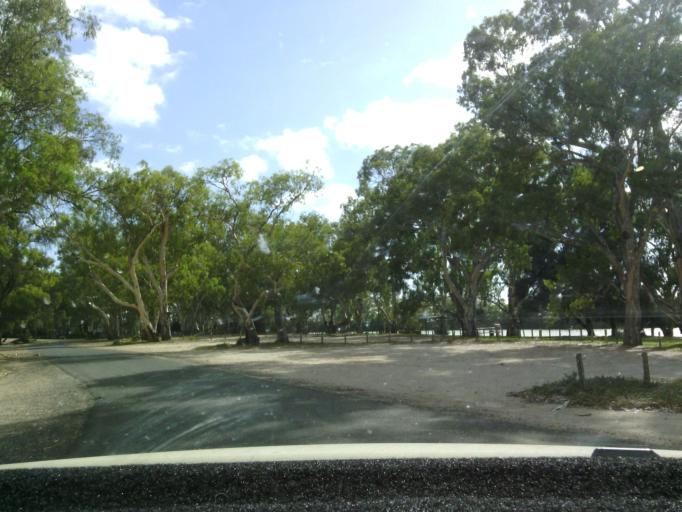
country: AU
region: South Australia
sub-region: Berri and Barmera
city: Berri
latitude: -34.2906
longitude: 140.6302
